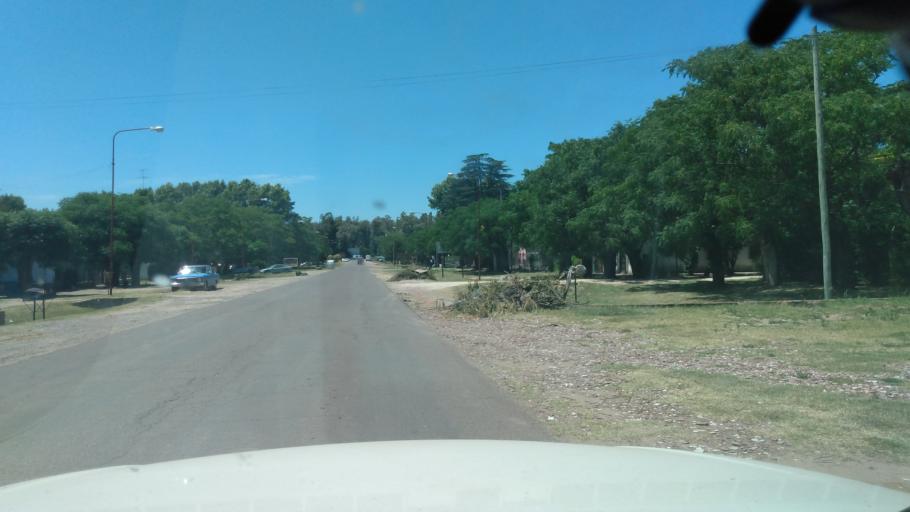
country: AR
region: Buenos Aires
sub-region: Partido de Lujan
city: Lujan
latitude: -34.5780
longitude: -59.1761
